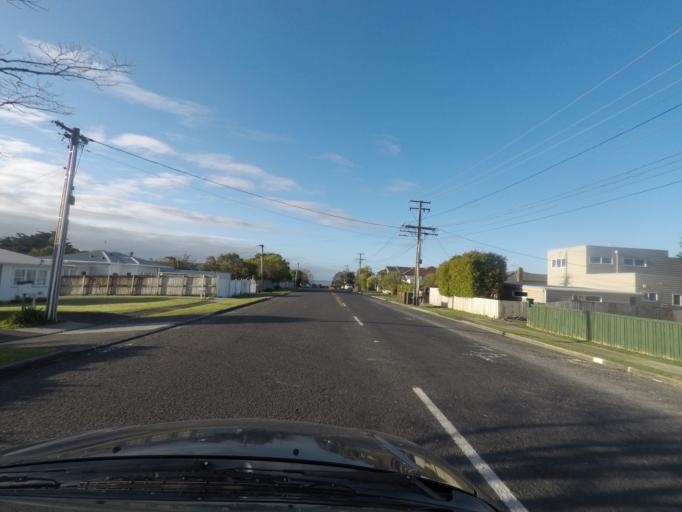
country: NZ
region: Auckland
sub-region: Auckland
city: Waitakere
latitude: -36.9144
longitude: 174.6582
